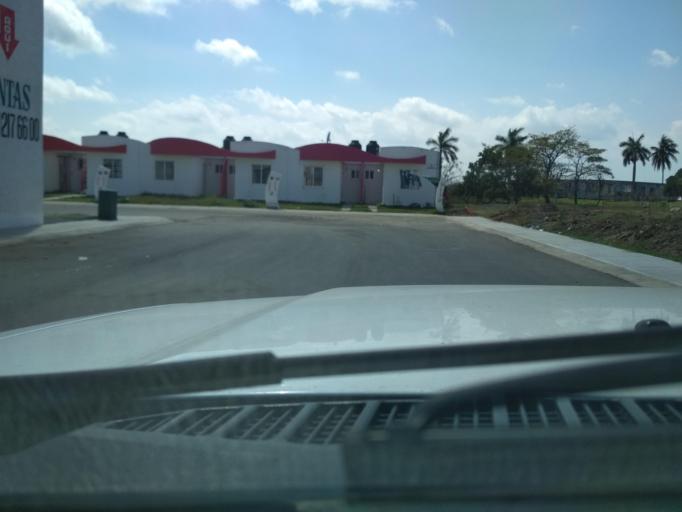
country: MX
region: Veracruz
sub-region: Veracruz
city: Las Amapolas
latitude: 19.1333
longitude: -96.2086
